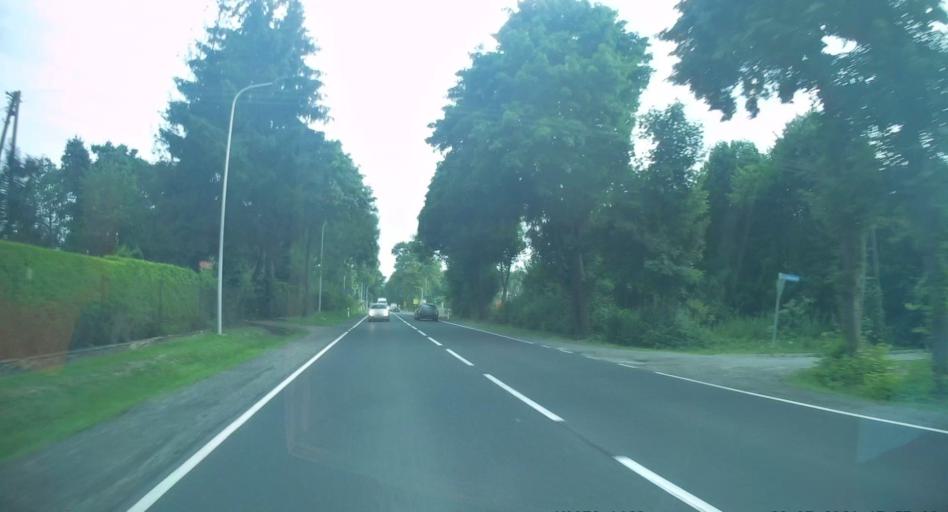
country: PL
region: Lodz Voivodeship
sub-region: Powiat radomszczanski
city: Gomunice
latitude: 51.1692
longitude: 19.4934
